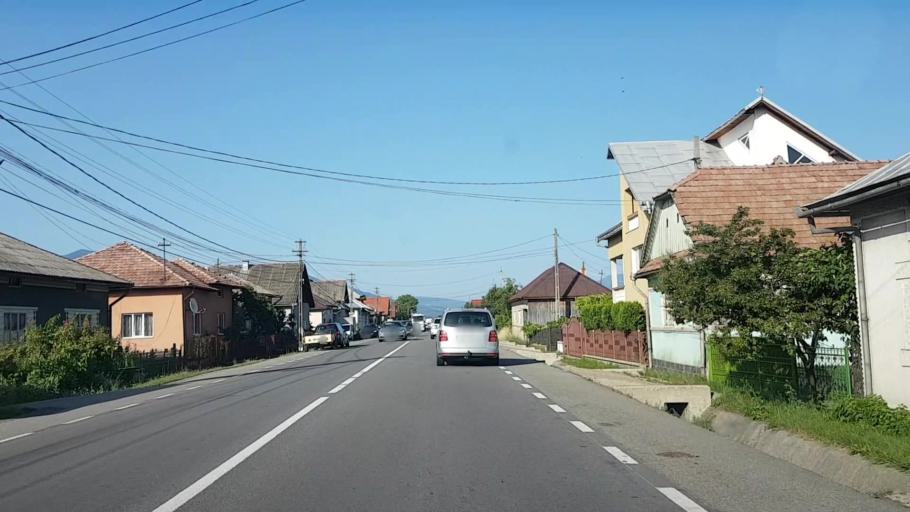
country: RO
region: Bistrita-Nasaud
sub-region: Comuna Josenii Bargaului
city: Josenii Bargaului
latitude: 47.1976
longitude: 24.6325
